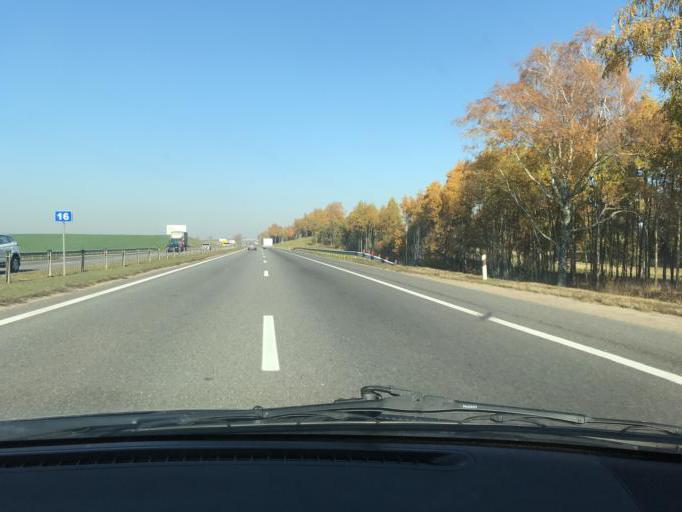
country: BY
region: Minsk
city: Samakhvalavichy
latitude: 53.7715
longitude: 27.5228
